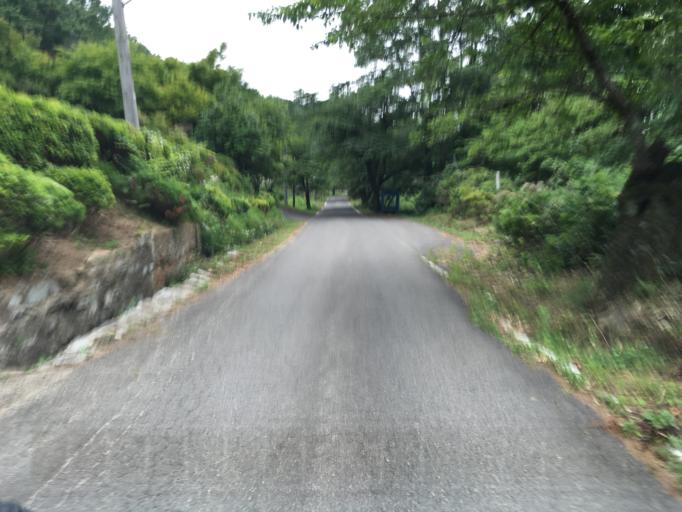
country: JP
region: Fukushima
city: Nihommatsu
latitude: 37.6473
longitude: 140.5290
